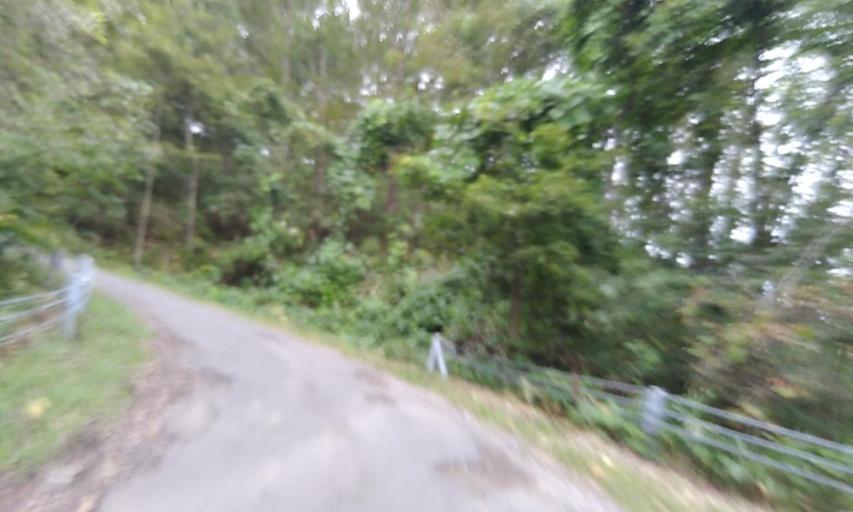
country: JP
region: Hokkaido
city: Obihiro
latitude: 42.8273
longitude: 142.9842
